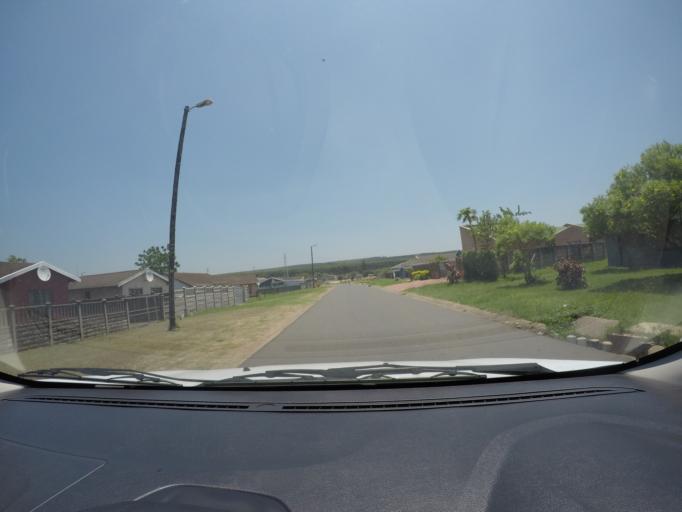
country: ZA
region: KwaZulu-Natal
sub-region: uThungulu District Municipality
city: eSikhawini
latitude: -28.8748
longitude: 31.8984
